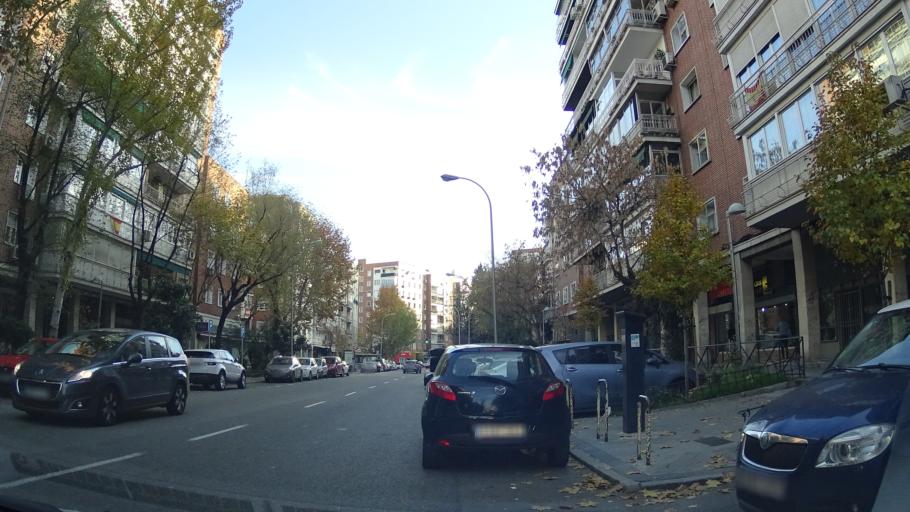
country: ES
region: Madrid
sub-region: Provincia de Madrid
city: Salamanca
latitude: 40.4402
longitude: -3.6630
